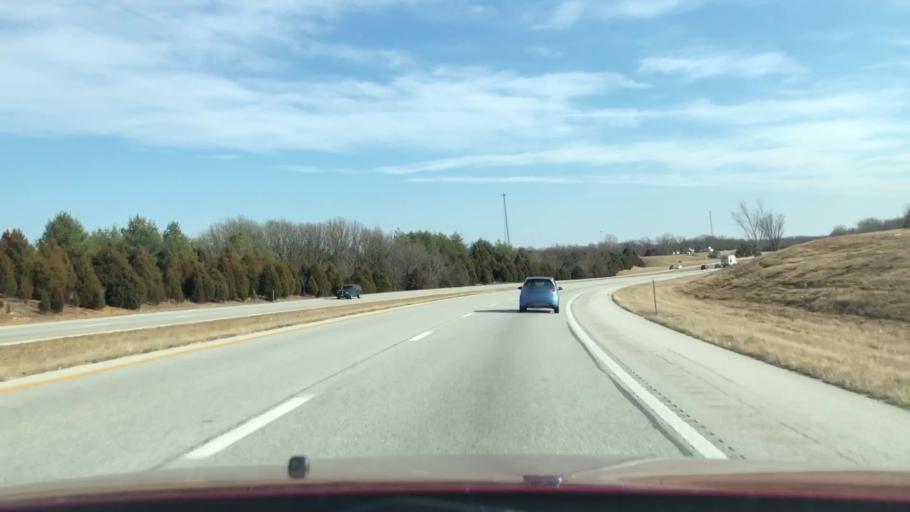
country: US
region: Missouri
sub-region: Webster County
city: Rogersville
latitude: 37.1509
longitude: -92.9491
